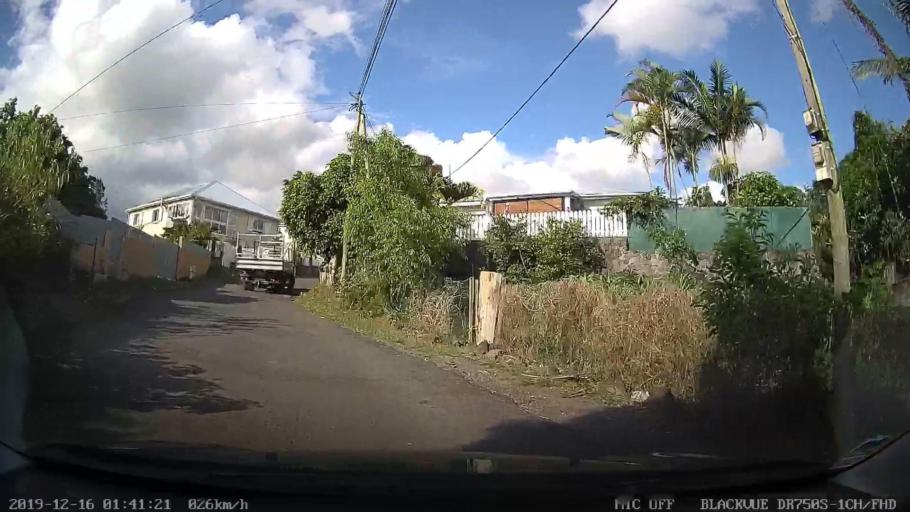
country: RE
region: Reunion
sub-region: Reunion
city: Le Tampon
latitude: -21.2562
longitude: 55.5086
